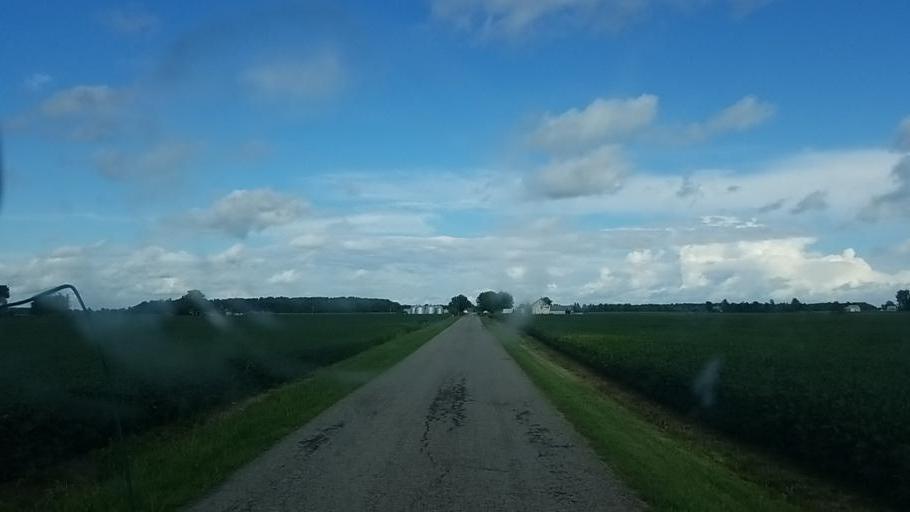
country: US
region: Ohio
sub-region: Hardin County
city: Forest
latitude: 40.7596
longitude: -83.4566
